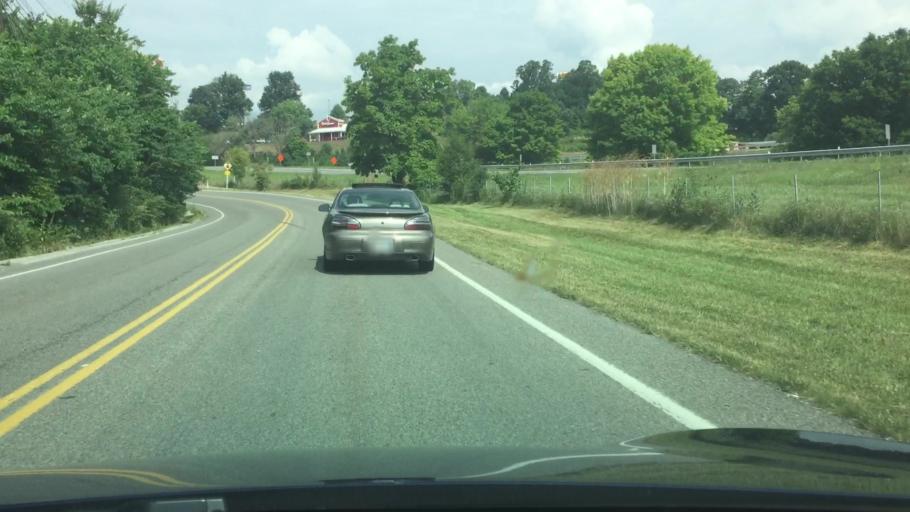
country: US
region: Virginia
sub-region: Wythe County
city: Wytheville
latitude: 36.9475
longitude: -81.0534
